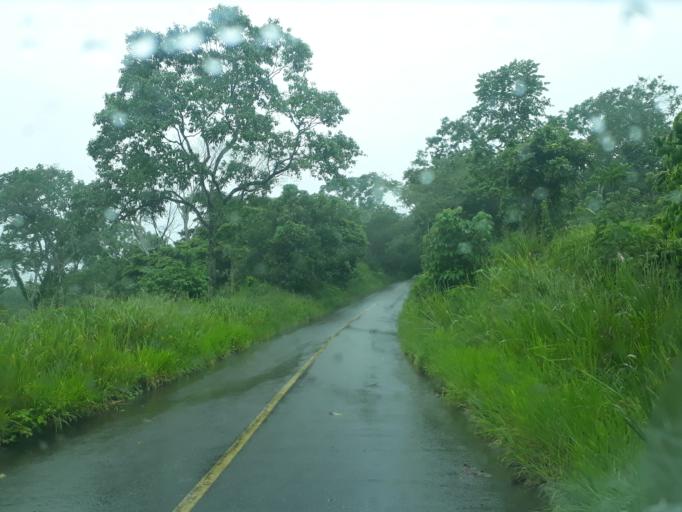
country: CO
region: Cundinamarca
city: Paratebueno
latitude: 4.4002
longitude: -73.3051
